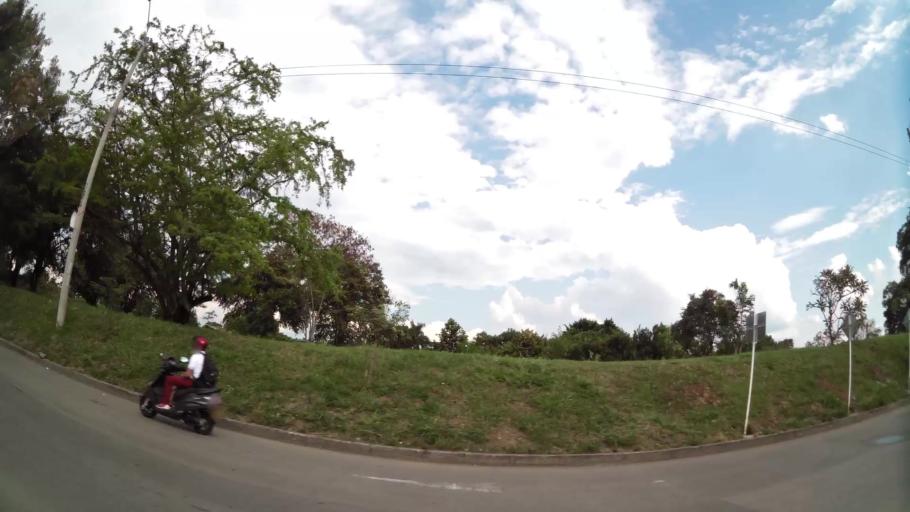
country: CO
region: Valle del Cauca
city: Cali
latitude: 3.4659
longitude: -76.5194
